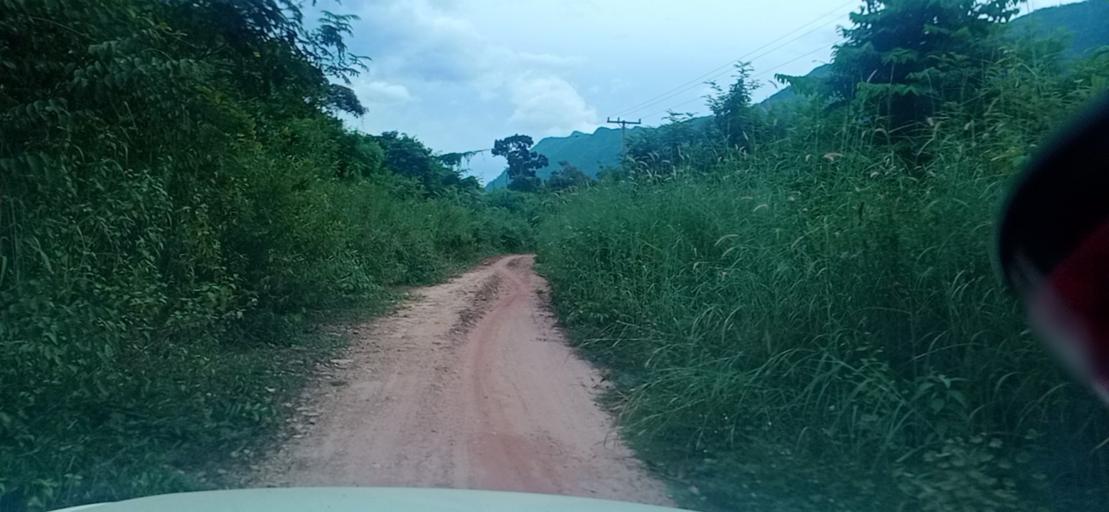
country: TH
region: Changwat Bueng Kan
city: Pak Khat
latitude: 18.5636
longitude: 103.2827
